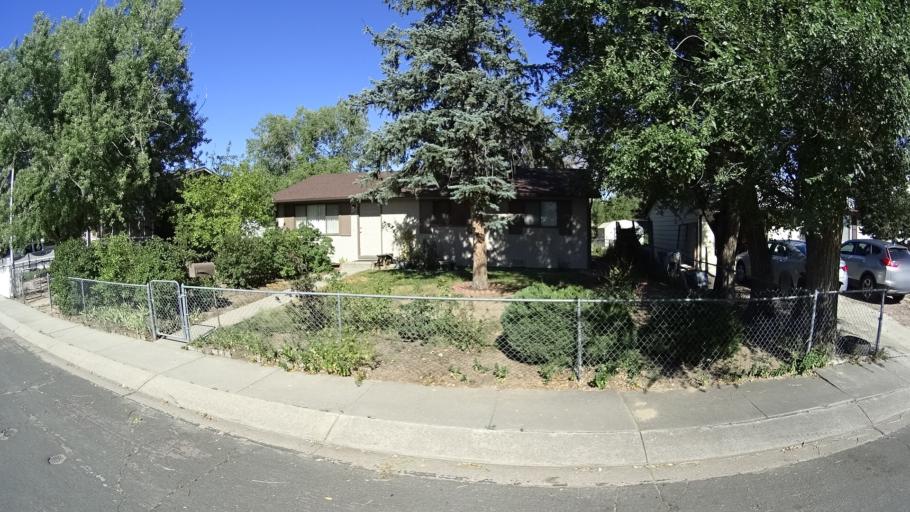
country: US
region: Colorado
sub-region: El Paso County
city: Stratmoor
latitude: 38.7958
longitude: -104.7478
